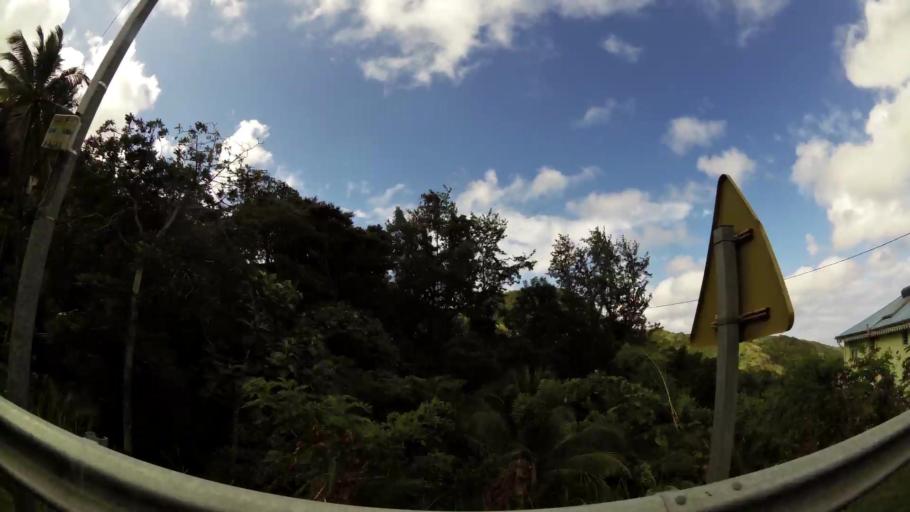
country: MQ
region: Martinique
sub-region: Martinique
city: Les Trois-Ilets
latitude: 14.5188
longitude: -61.0744
